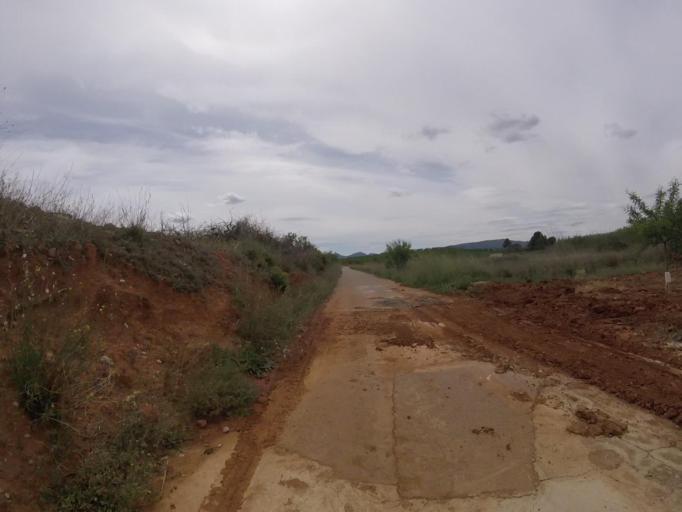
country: ES
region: Valencia
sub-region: Provincia de Castello
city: Benlloch
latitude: 40.1854
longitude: -0.0090
